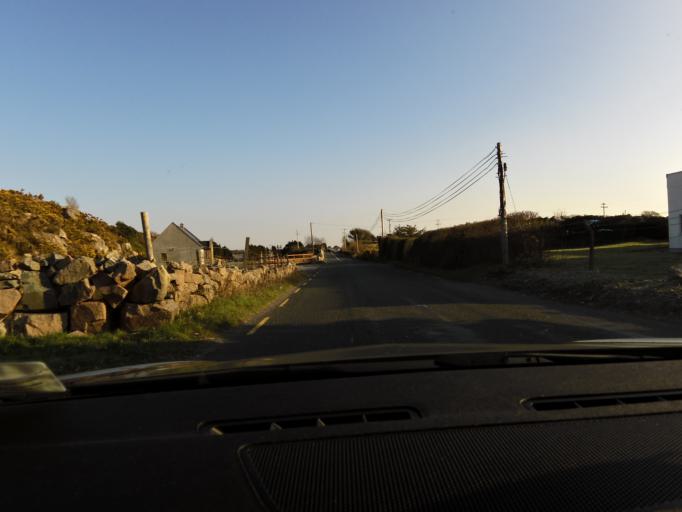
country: IE
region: Connaught
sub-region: County Galway
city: Oughterard
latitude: 53.2909
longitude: -9.5492
